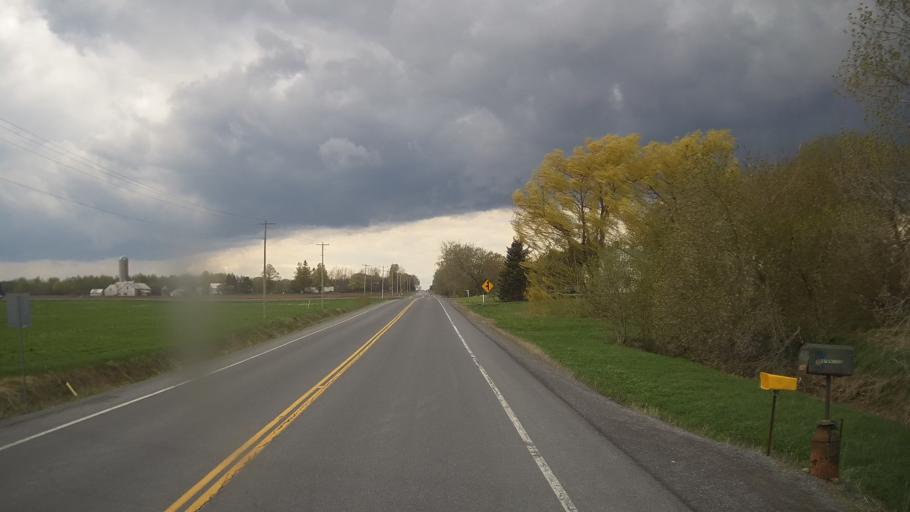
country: CA
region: Ontario
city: Hawkesbury
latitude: 45.5346
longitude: -74.5542
